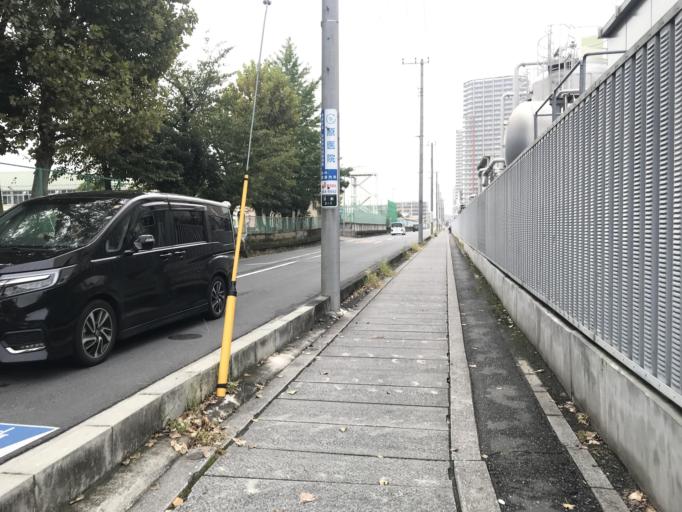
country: JP
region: Saitama
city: Shimotoda
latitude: 35.8388
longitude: 139.6475
